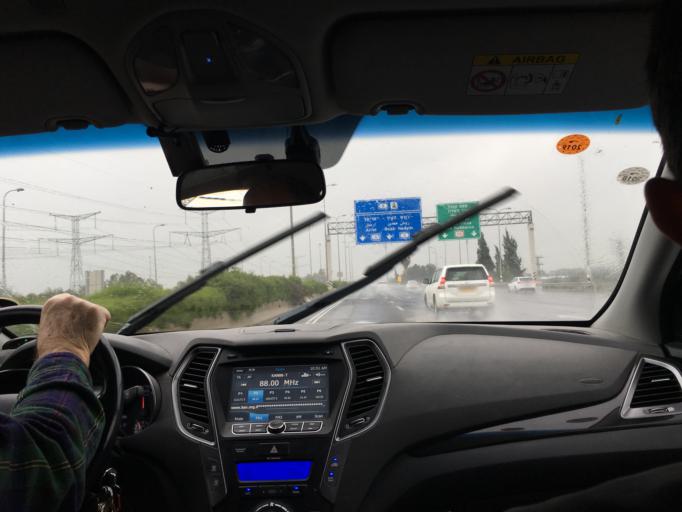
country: IL
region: Central District
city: Petah Tiqwa
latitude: 32.1221
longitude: 34.8984
